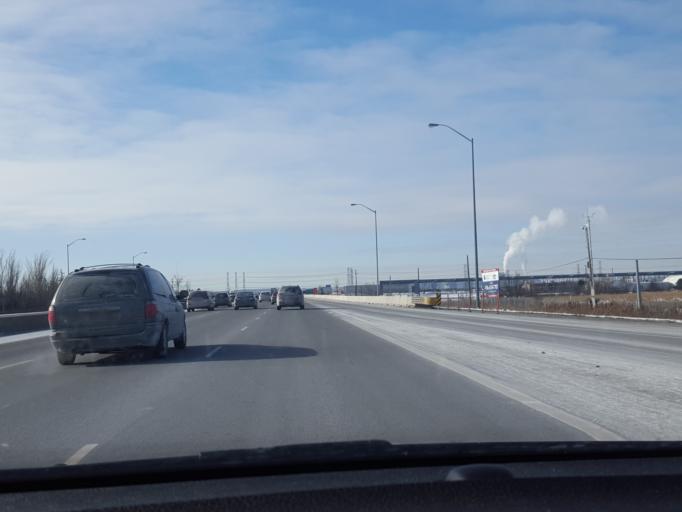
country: CA
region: Ontario
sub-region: Halton
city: Milton
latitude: 43.5549
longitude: -79.8477
